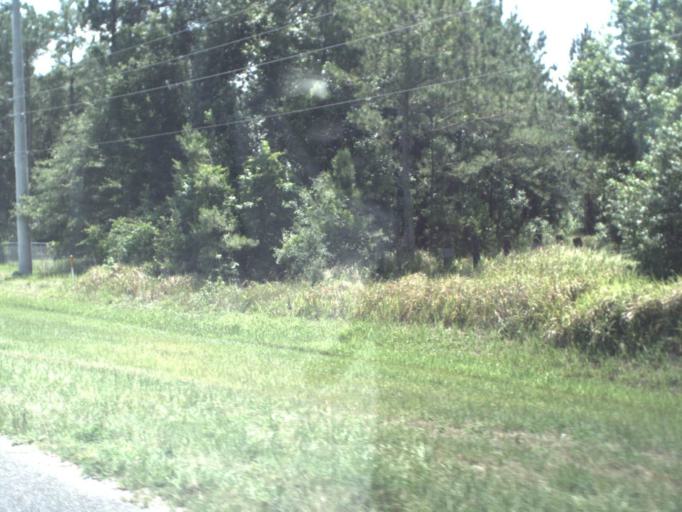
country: US
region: Florida
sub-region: Putnam County
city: East Palatka
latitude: 29.7378
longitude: -81.4753
